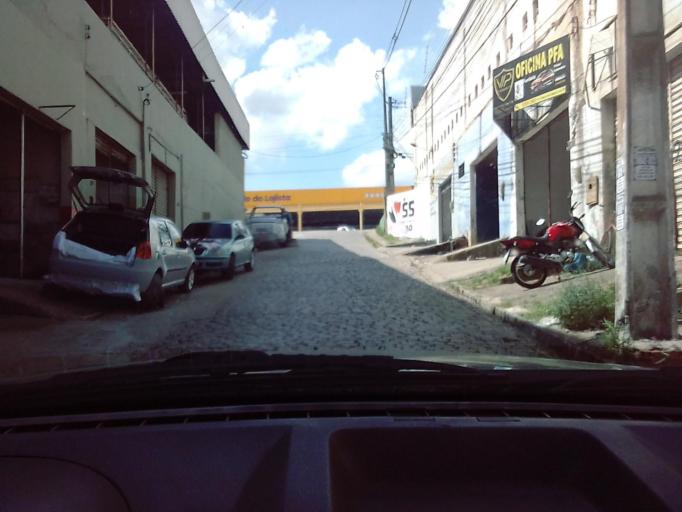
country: BR
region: Pernambuco
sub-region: Vitoria De Santo Antao
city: Vitoria de Santo Antao
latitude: -8.1180
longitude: -35.3091
